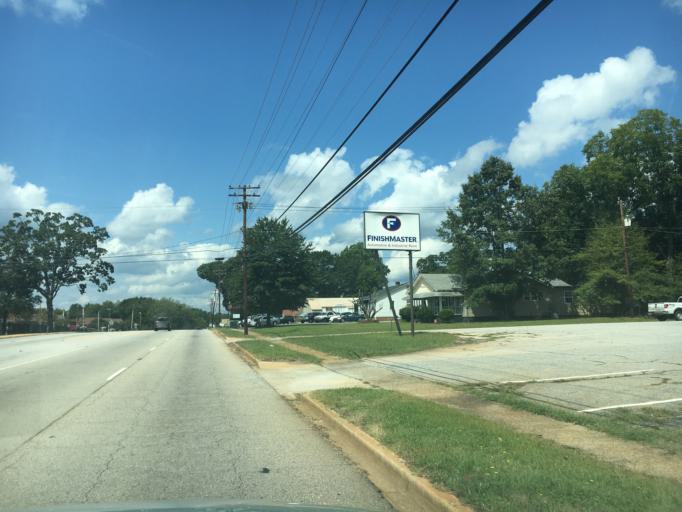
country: US
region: South Carolina
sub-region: Greenville County
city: City View
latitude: 34.8728
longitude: -82.4375
